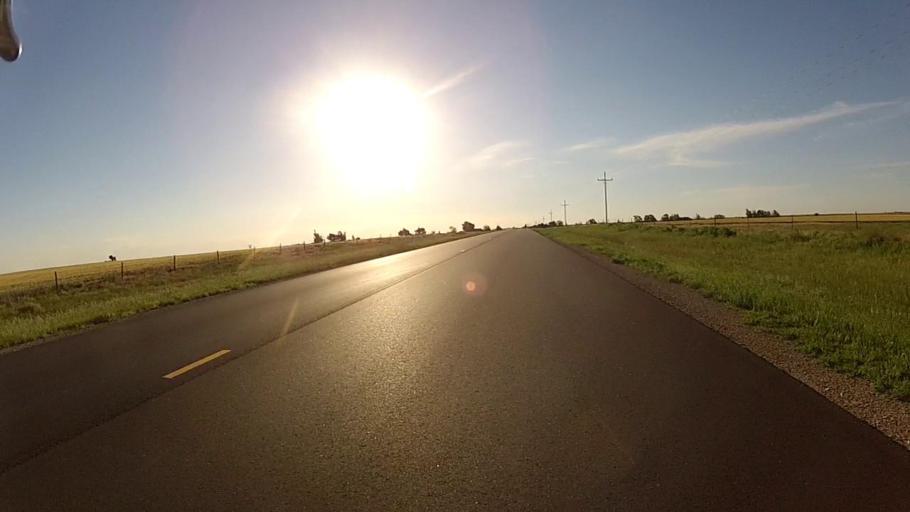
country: US
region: Kansas
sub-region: Comanche County
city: Coldwater
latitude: 37.2816
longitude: -99.1778
